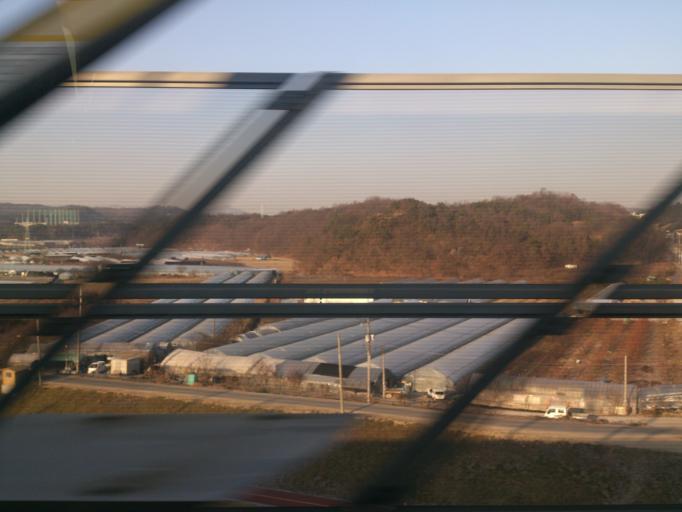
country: KR
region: Daejeon
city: Songgang-dong
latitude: 36.4093
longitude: 127.4151
